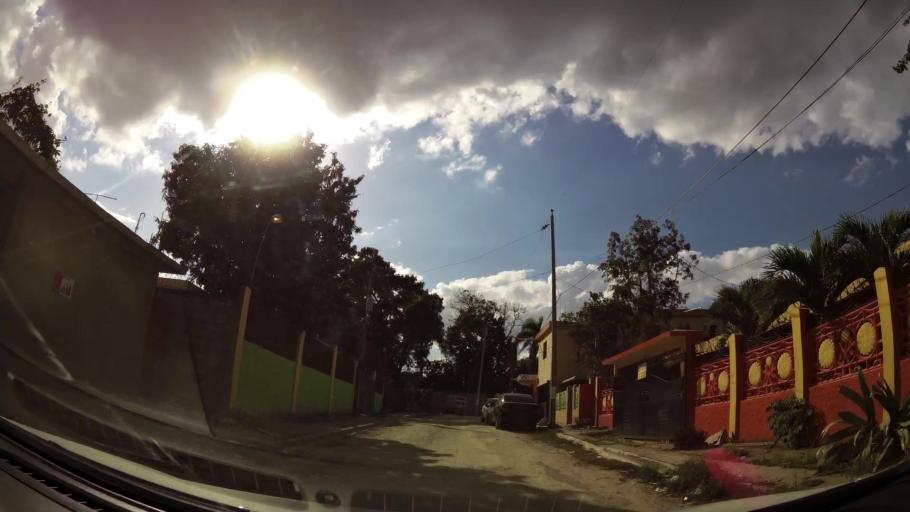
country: DO
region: Nacional
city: Ensanche Luperon
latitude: 18.5570
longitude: -69.9005
